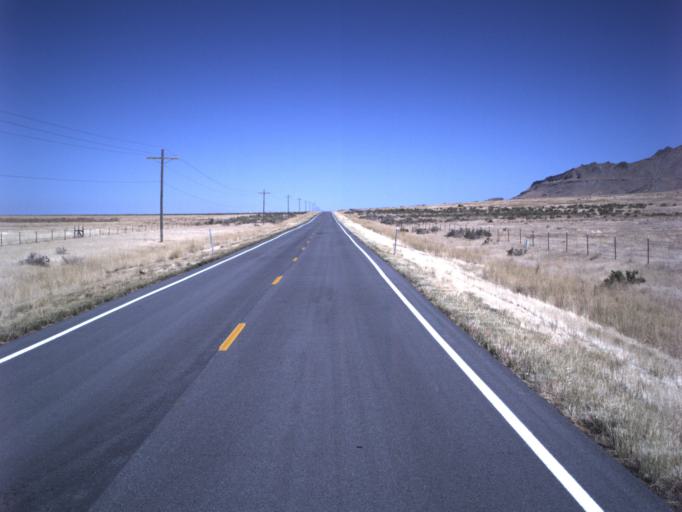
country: US
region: Utah
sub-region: Tooele County
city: Grantsville
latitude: 40.6888
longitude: -112.6690
